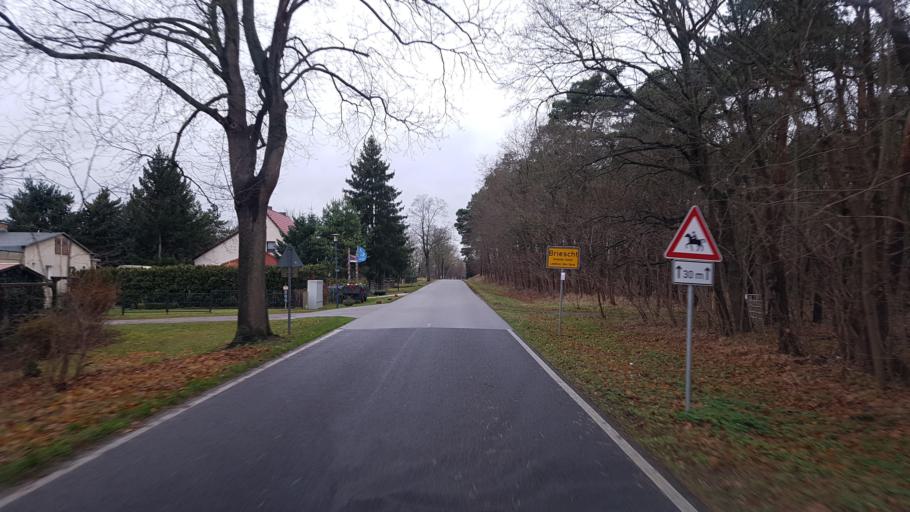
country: DE
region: Brandenburg
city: Tauche
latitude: 52.1052
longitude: 14.1325
